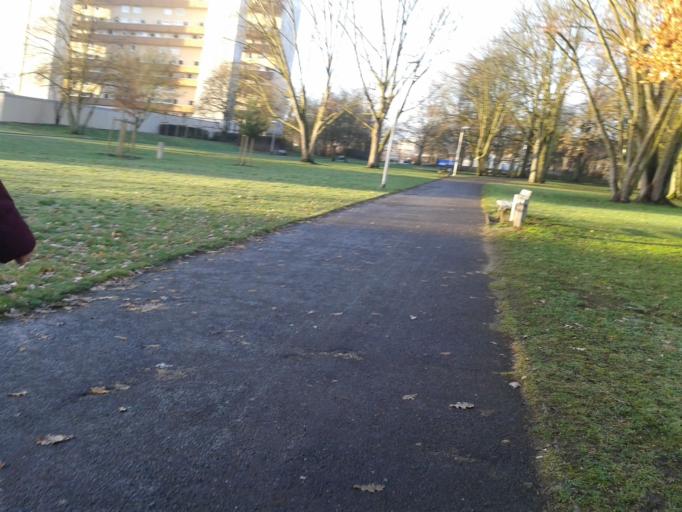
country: DE
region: Bavaria
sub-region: Upper Franconia
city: Bamberg
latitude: 49.9079
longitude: 10.9088
